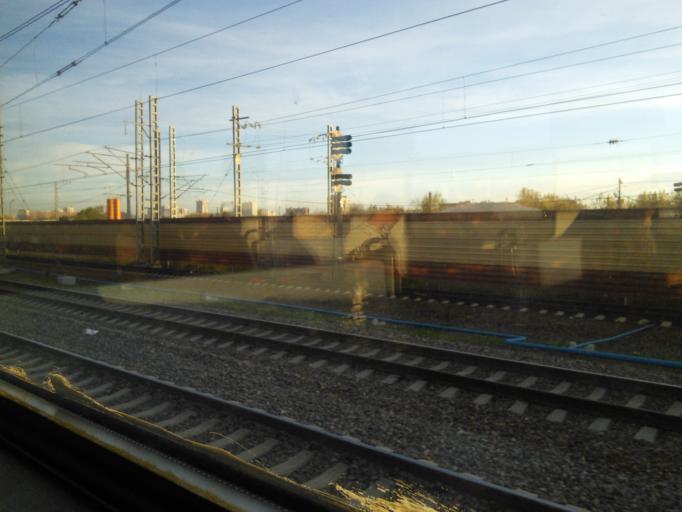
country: RU
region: Moscow
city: Zapadnoye Degunino
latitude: 55.8560
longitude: 37.5418
